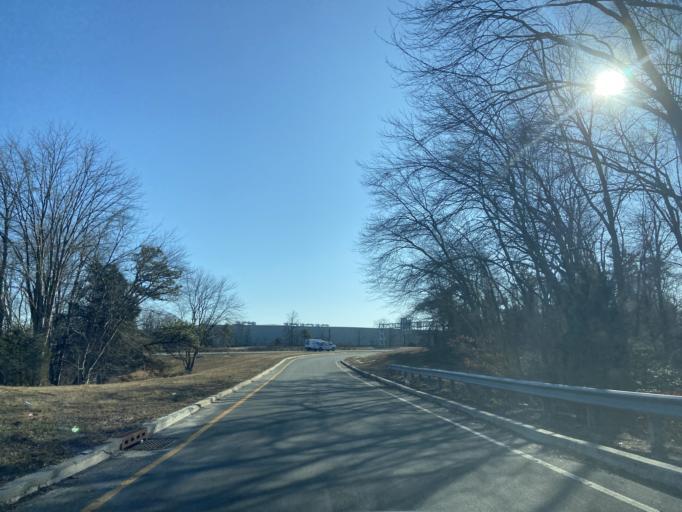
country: US
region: New Jersey
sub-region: Gloucester County
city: Newfield
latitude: 39.5207
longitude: -75.0705
